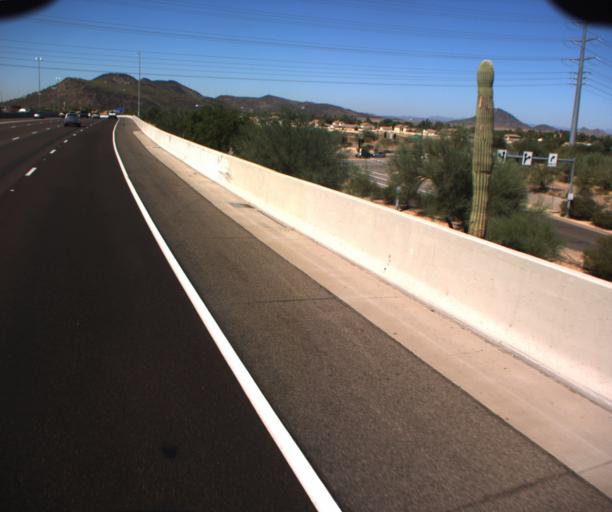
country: US
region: Arizona
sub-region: Maricopa County
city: Peoria
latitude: 33.6691
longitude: -112.1333
